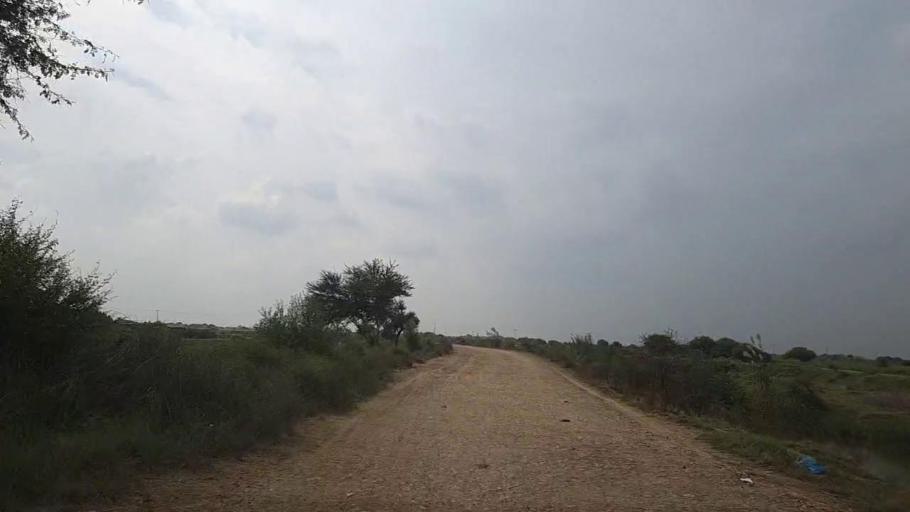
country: PK
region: Sindh
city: Mirpur Batoro
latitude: 24.5861
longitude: 68.1219
